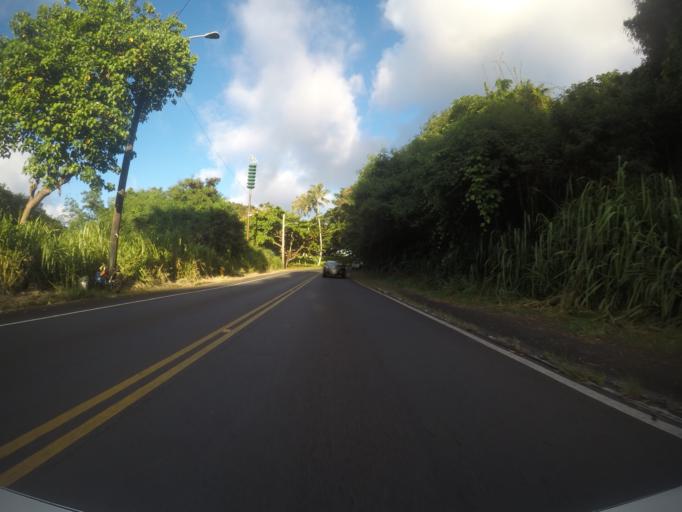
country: US
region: Hawaii
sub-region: Honolulu County
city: He'eia
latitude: 21.4417
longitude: -157.8107
